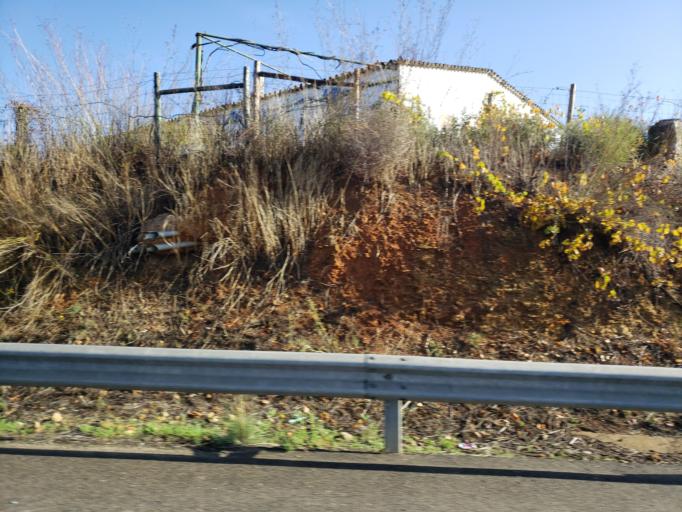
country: PT
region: Faro
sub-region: Portimao
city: Portimao
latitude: 37.1621
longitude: -8.5691
